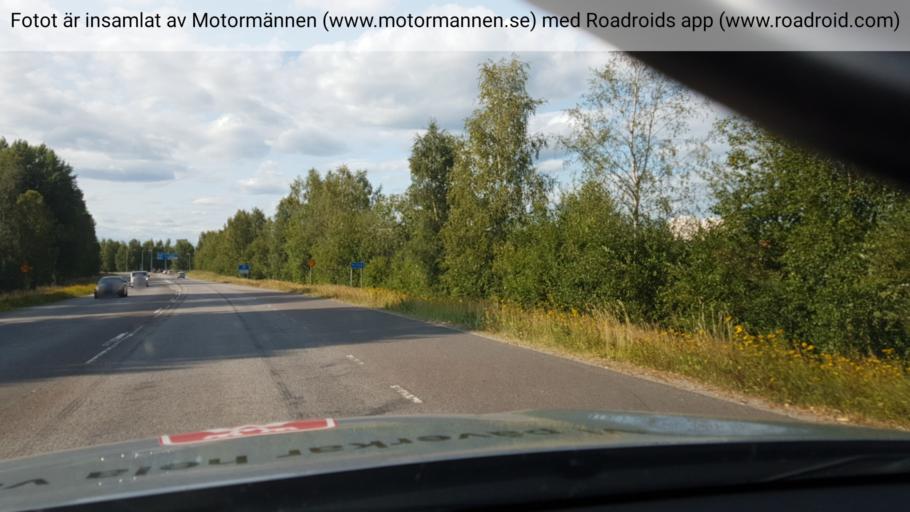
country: SE
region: Norrbotten
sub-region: Pitea Kommun
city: Pitea
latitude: 65.3079
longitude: 21.5036
